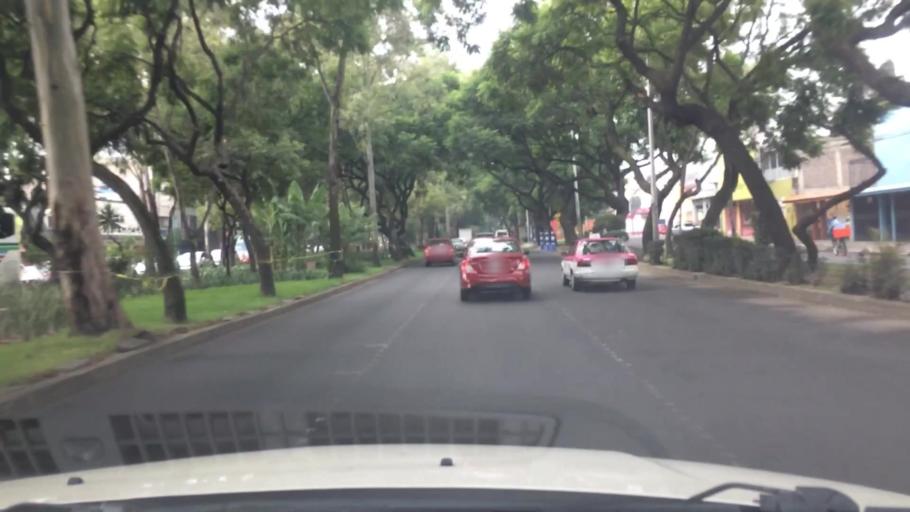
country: MX
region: Mexico City
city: Coyoacan
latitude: 19.3292
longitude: -99.1370
